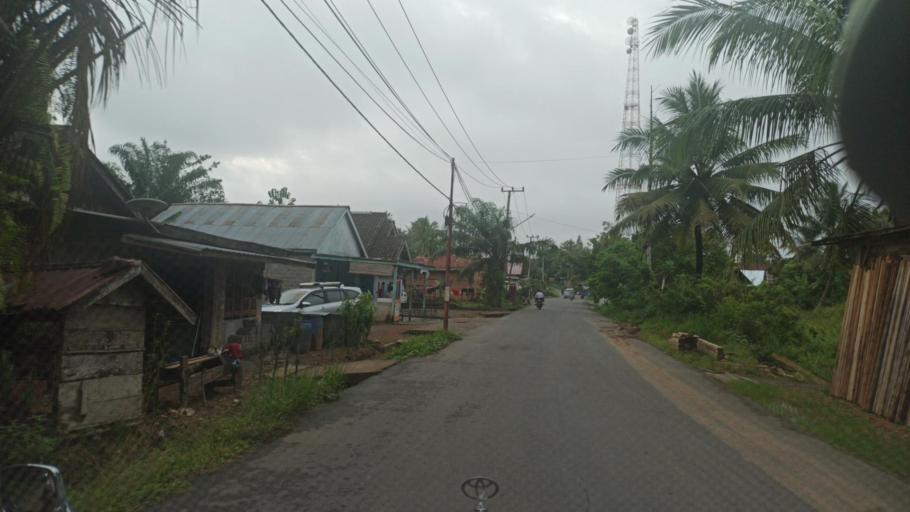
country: ID
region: South Sumatra
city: Gunungmegang Dalam
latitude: -3.2687
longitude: 103.8266
